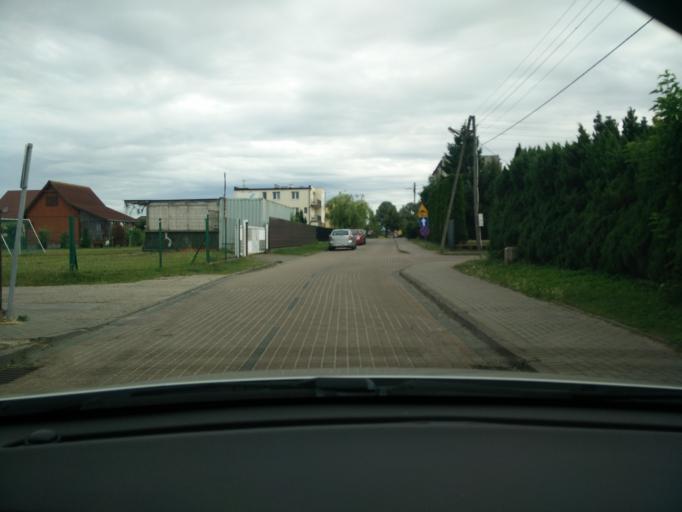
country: PL
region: Pomeranian Voivodeship
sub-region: Powiat pucki
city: Mosty
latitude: 54.6316
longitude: 18.5042
